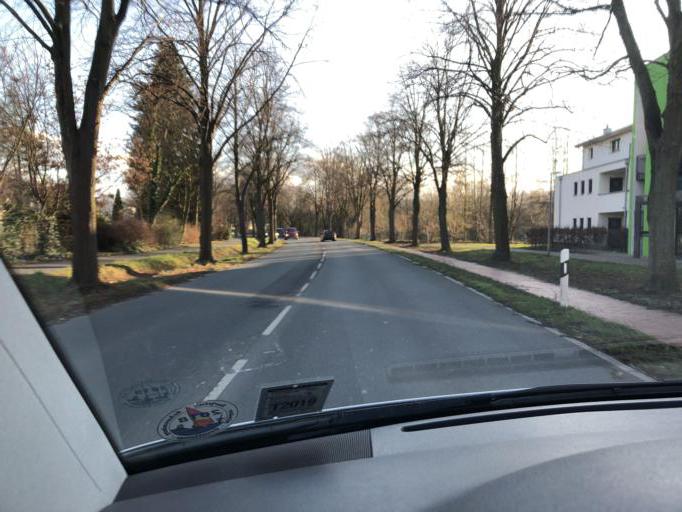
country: DE
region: North Rhine-Westphalia
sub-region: Regierungsbezirk Arnsberg
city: Soest
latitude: 51.5730
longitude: 8.0905
